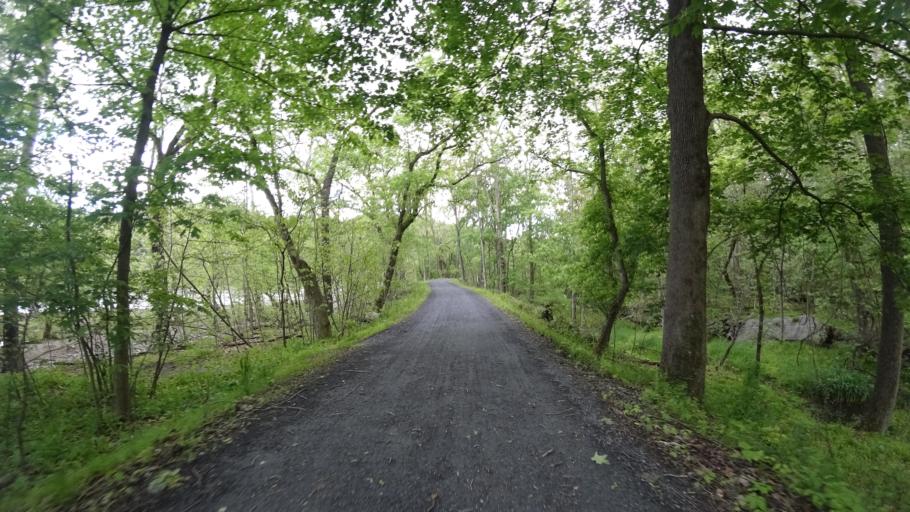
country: US
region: West Virginia
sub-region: Jefferson County
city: Bolivar
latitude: 39.3364
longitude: -77.7509
